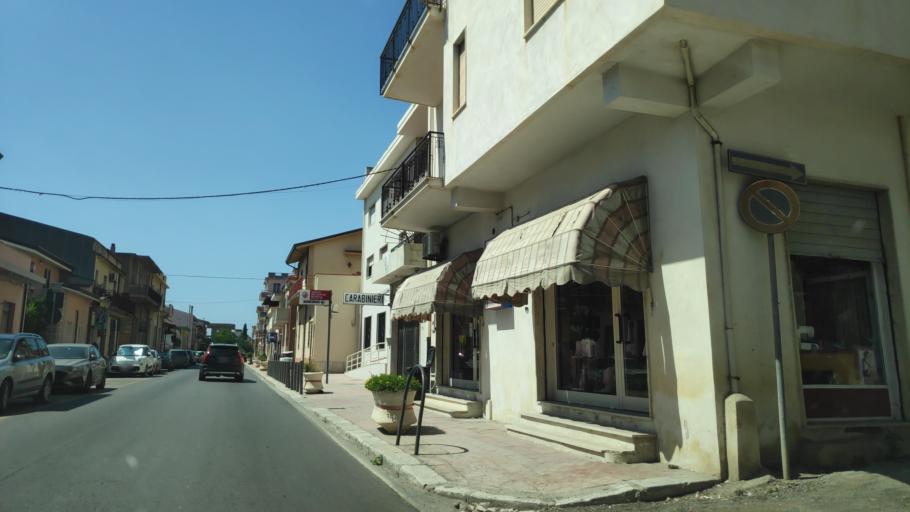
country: IT
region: Calabria
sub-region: Provincia di Reggio Calabria
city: Brancaleone
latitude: 37.9642
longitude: 16.1018
